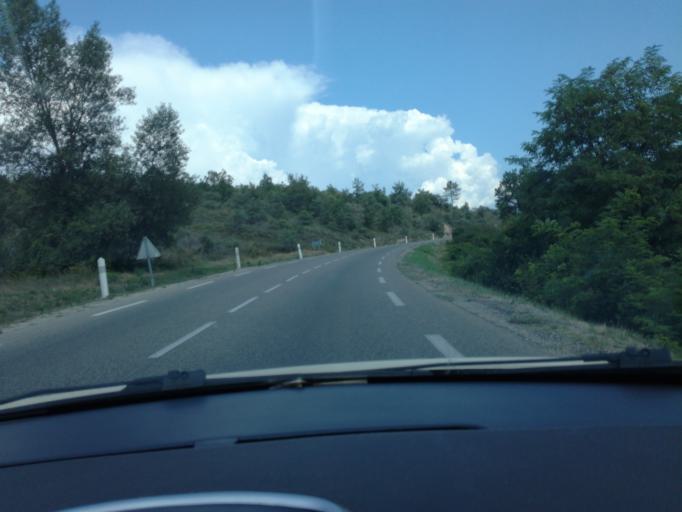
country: FR
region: Rhone-Alpes
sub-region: Departement de l'Ardeche
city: Ruoms
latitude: 44.4932
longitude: 4.3807
